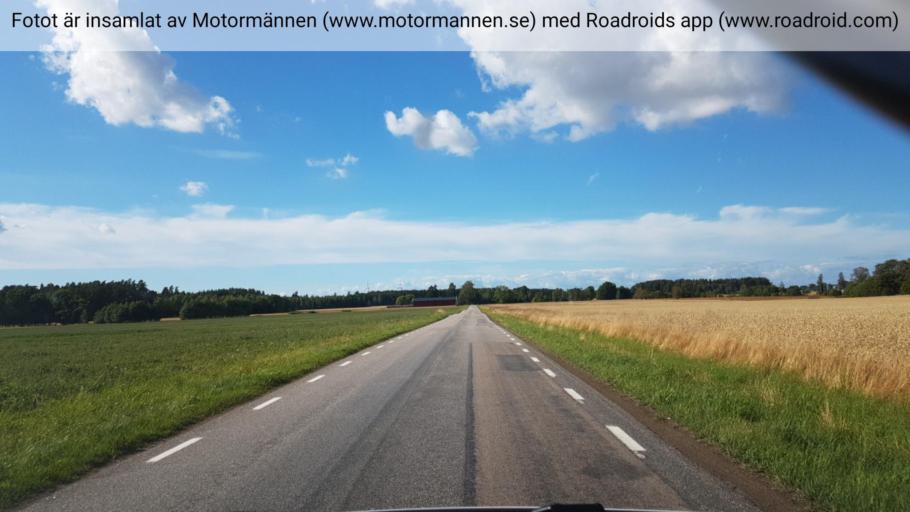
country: SE
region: Vaestra Goetaland
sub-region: Gotene Kommun
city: Kallby
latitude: 58.4747
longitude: 13.3252
